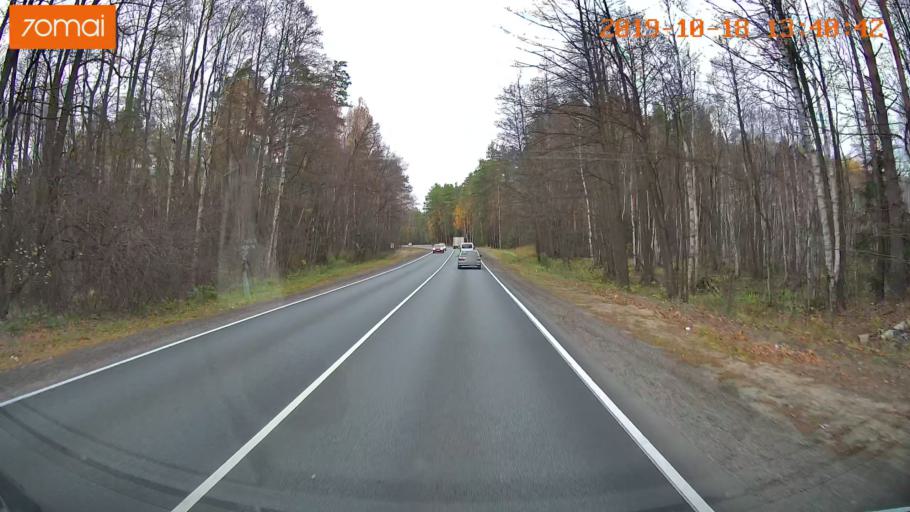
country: RU
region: Rjazan
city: Solotcha
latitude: 54.9127
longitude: 39.9979
